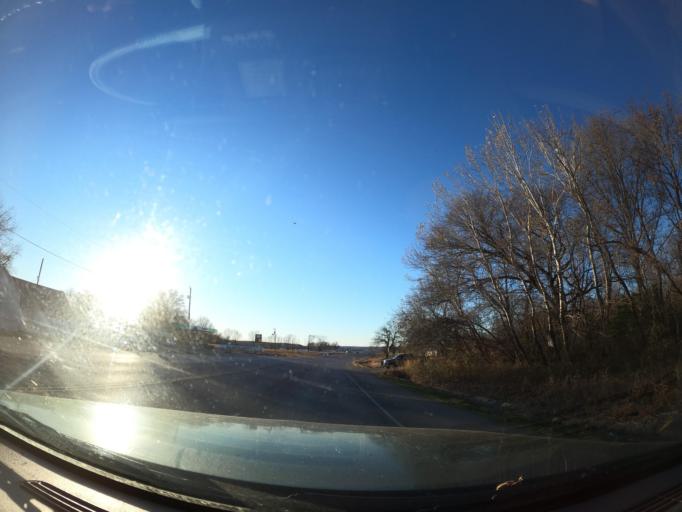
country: US
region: Oklahoma
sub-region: Pittsburg County
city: Krebs
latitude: 34.8942
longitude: -95.6491
